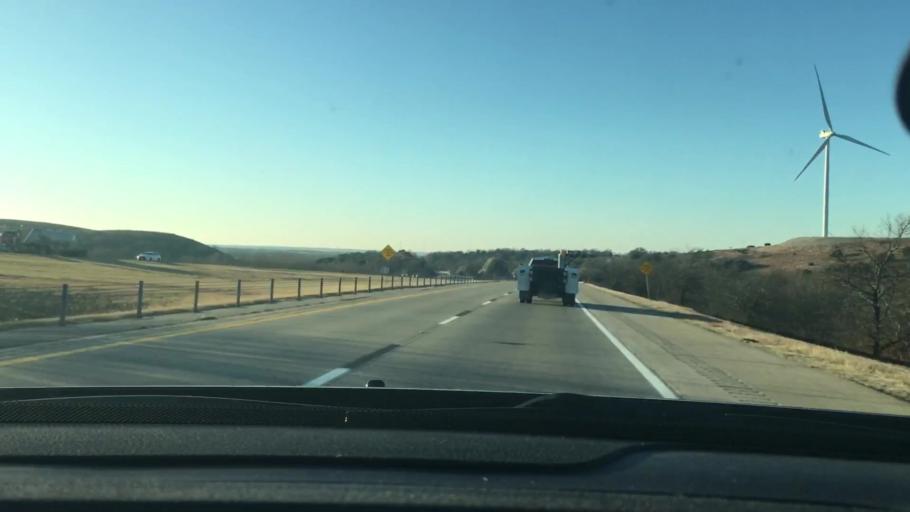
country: US
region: Oklahoma
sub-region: Murray County
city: Davis
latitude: 34.3637
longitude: -97.1477
